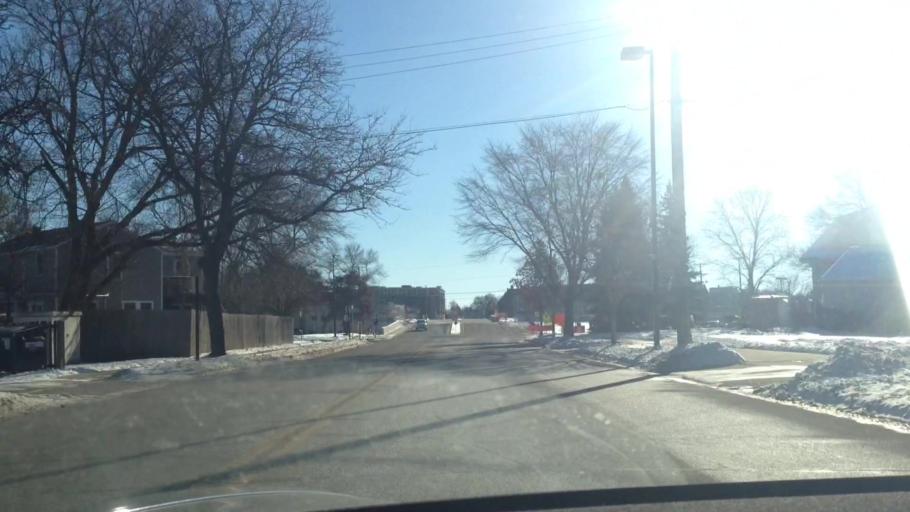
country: US
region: Minnesota
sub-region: Hennepin County
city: Saint Louis Park
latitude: 44.9407
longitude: -93.3585
